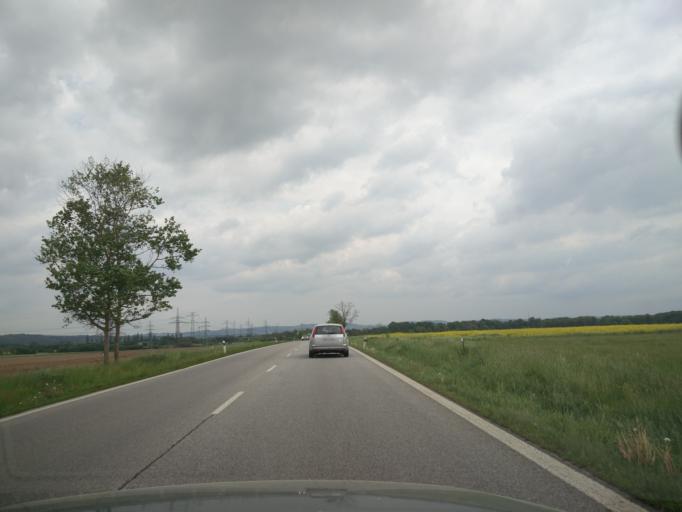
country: CZ
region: Jihocesky
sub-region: Okres Ceske Budejovice
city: Hluboka nad Vltavou
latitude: 49.0177
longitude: 14.4212
